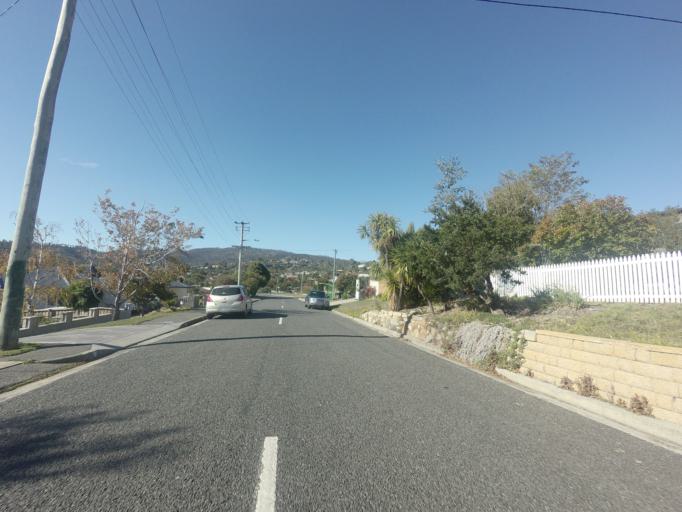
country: AU
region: Tasmania
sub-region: Clarence
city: Lindisfarne
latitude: -42.8400
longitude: 147.3494
